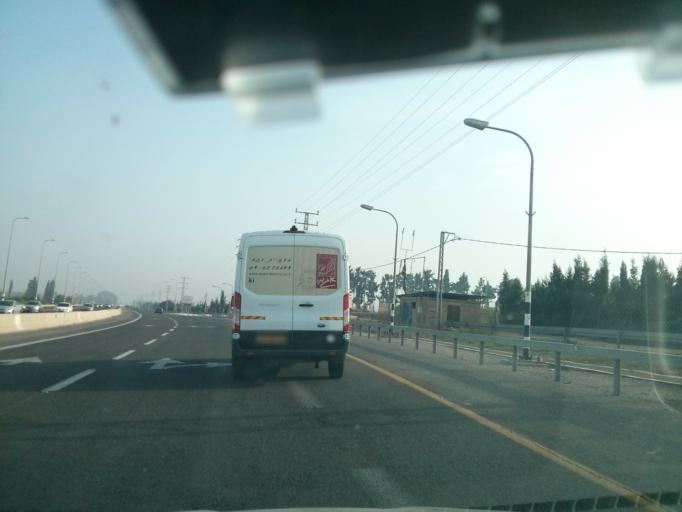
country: IL
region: Haifa
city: Qesarya
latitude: 32.5070
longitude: 34.9307
